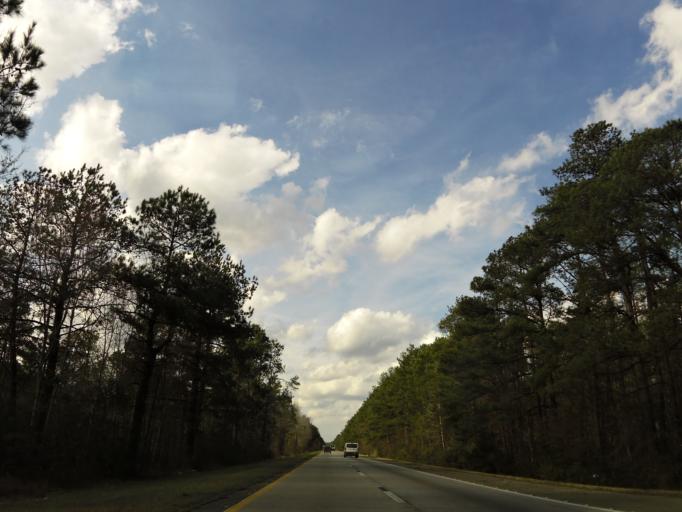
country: US
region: South Carolina
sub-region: Orangeburg County
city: Holly Hill
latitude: 33.2101
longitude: -80.4106
